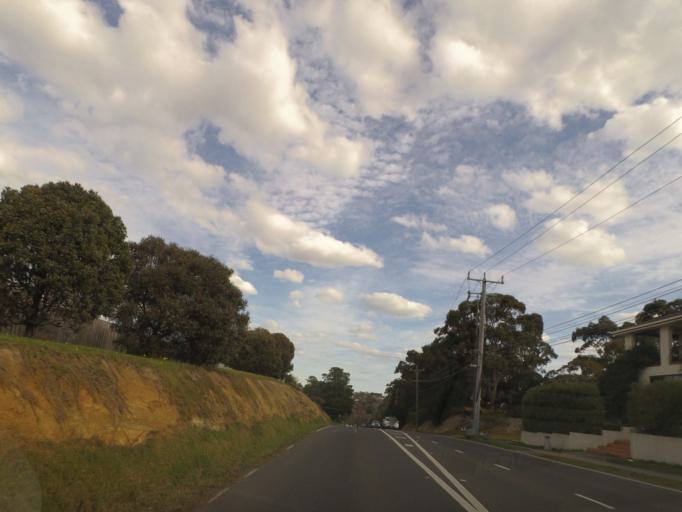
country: AU
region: Victoria
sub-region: Manningham
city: Doncaster East
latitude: -37.7749
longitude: 145.1458
